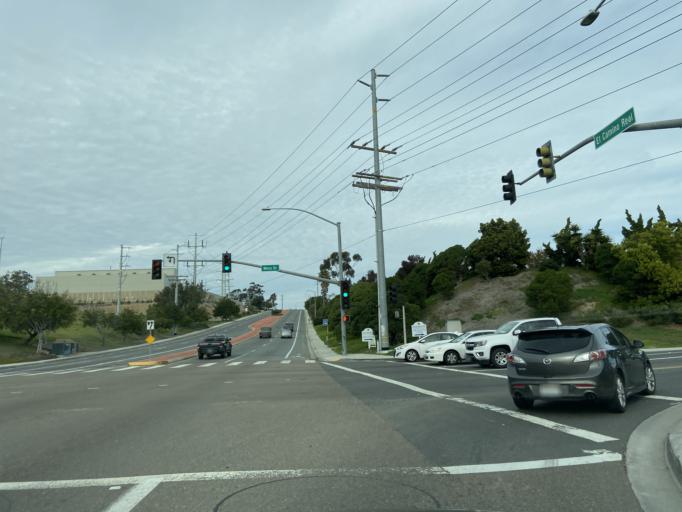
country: US
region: California
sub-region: San Diego County
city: Oceanside
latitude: 33.2085
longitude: -117.3334
